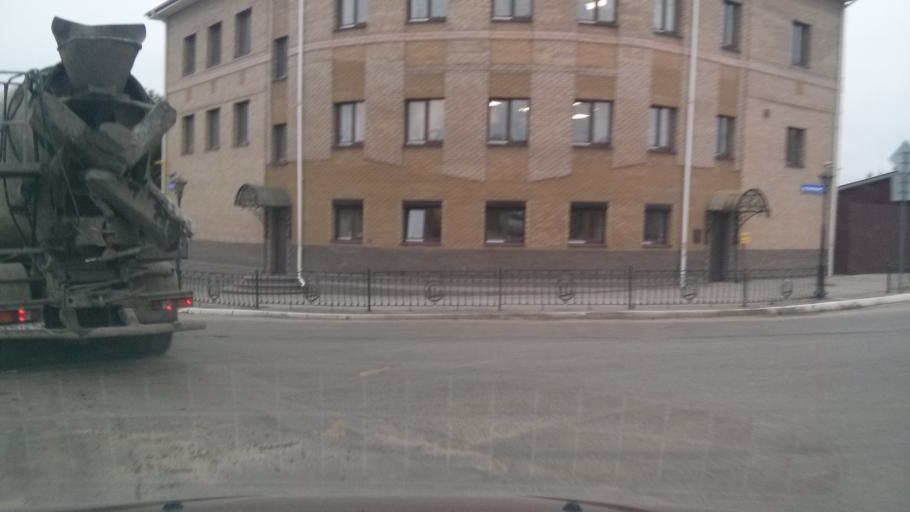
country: RU
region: Nizjnij Novgorod
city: Nizhniy Novgorod
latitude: 56.3022
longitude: 44.0103
